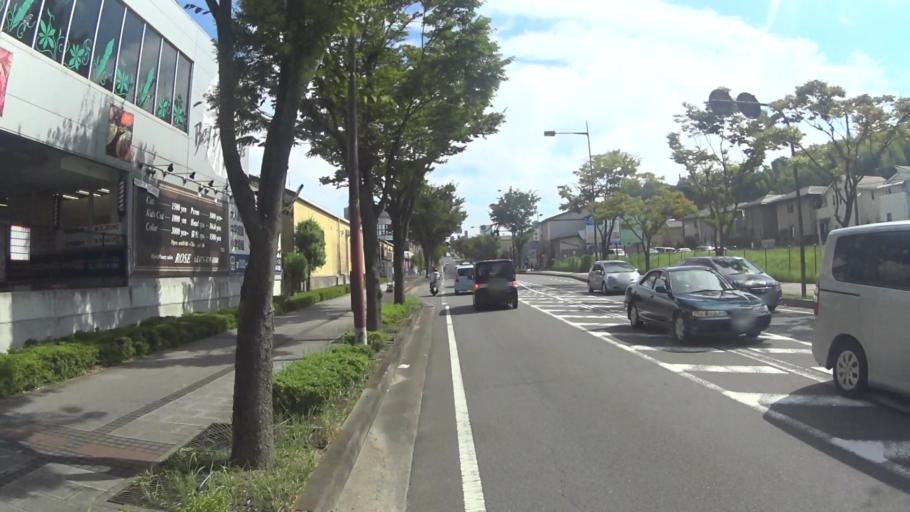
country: JP
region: Kyoto
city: Yawata
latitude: 34.8401
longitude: 135.7153
